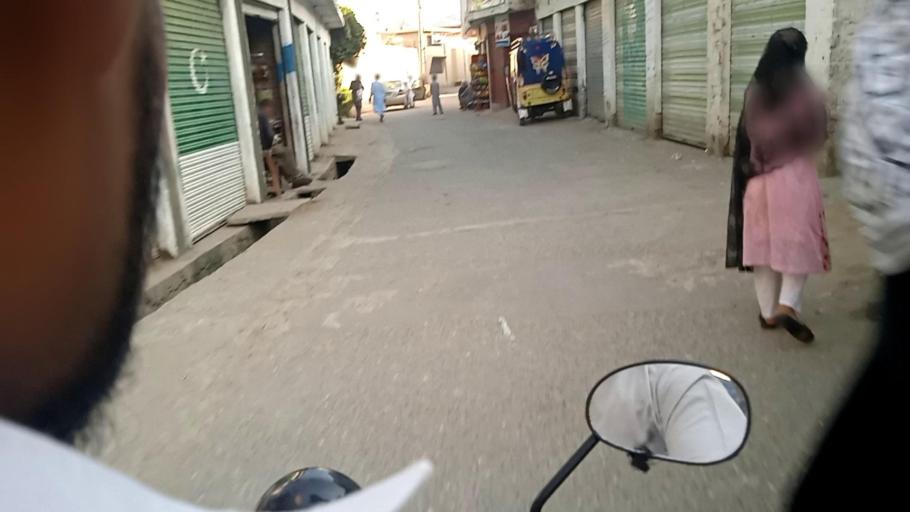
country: PK
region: Khyber Pakhtunkhwa
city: Mingora
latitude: 34.8097
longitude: 72.3610
